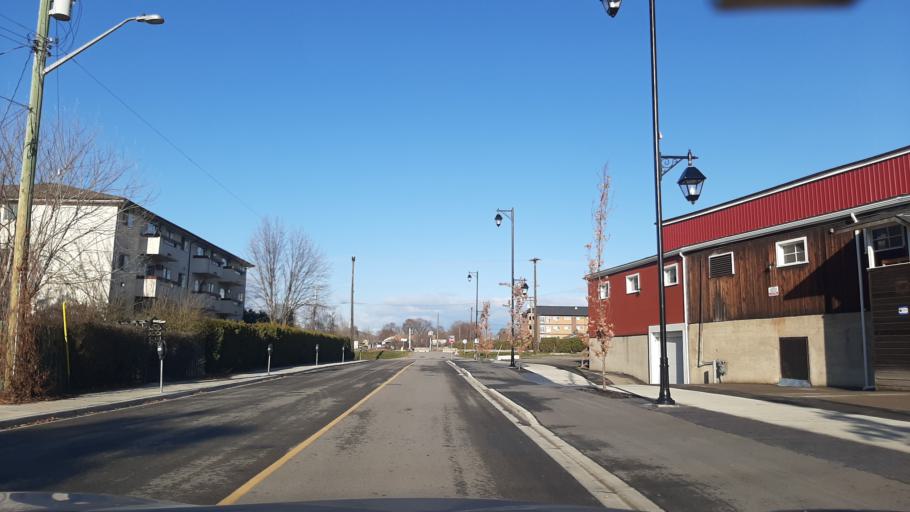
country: CA
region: British Columbia
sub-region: Regional District of North Okanagan
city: Vernon
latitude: 50.2680
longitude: -119.2708
